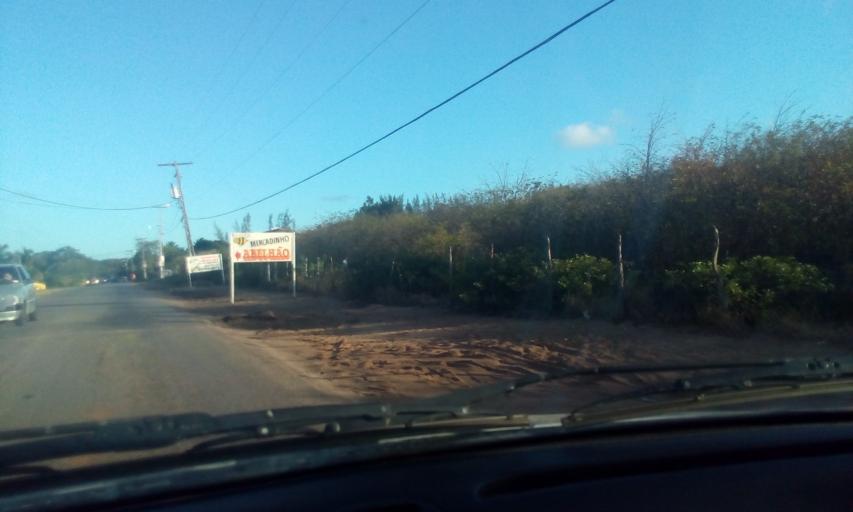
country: BR
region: Rio Grande do Norte
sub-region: Parnamirim
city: Parnamirim
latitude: -5.9551
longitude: -35.1716
